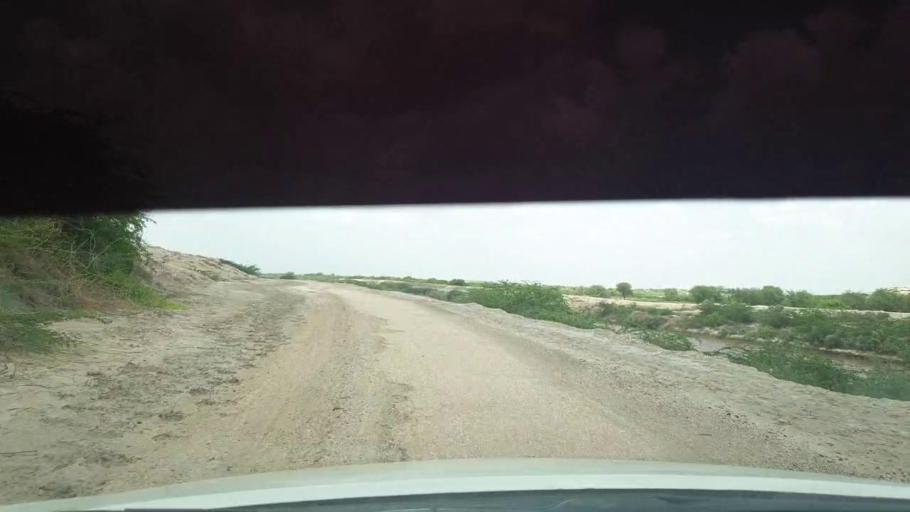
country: PK
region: Sindh
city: Kadhan
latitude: 24.5070
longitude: 69.1181
